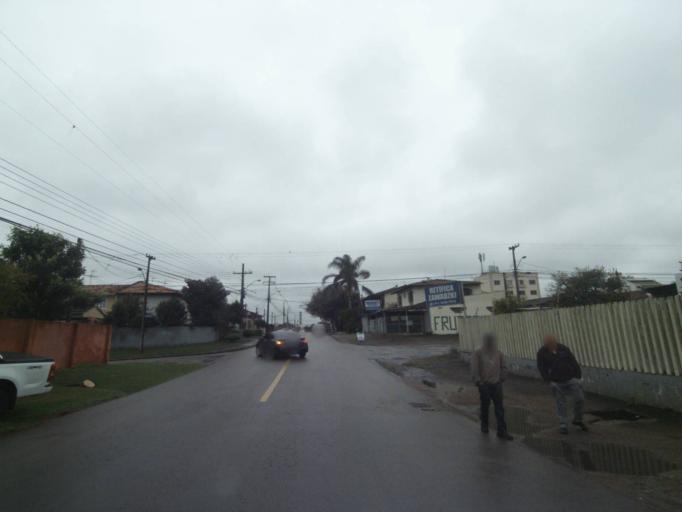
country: BR
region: Parana
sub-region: Curitiba
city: Curitiba
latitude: -25.5097
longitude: -49.3009
